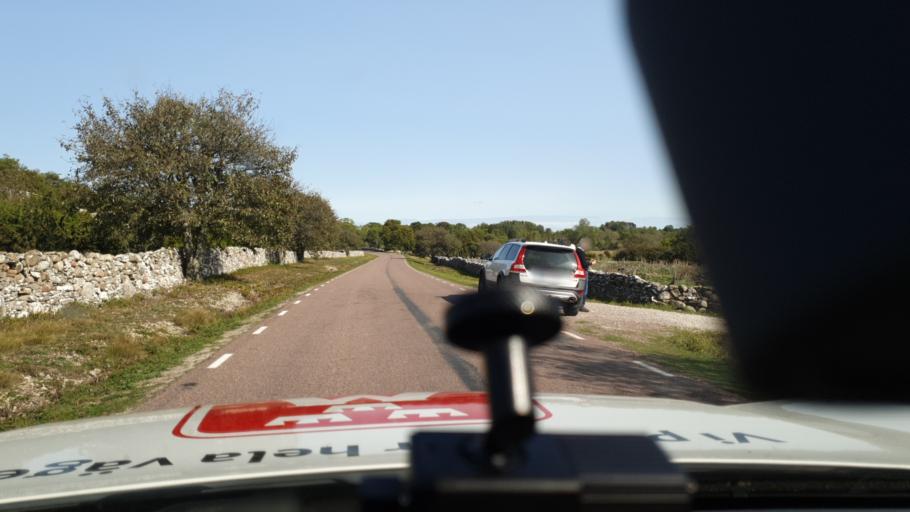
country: SE
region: Gotland
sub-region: Gotland
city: Hemse
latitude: 56.9177
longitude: 18.1549
